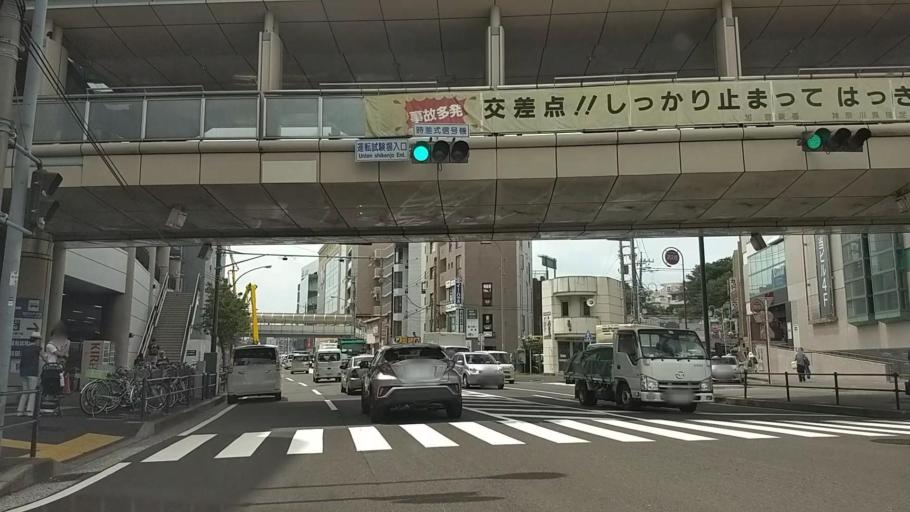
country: JP
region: Kanagawa
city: Minami-rinkan
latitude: 35.4644
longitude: 139.5326
